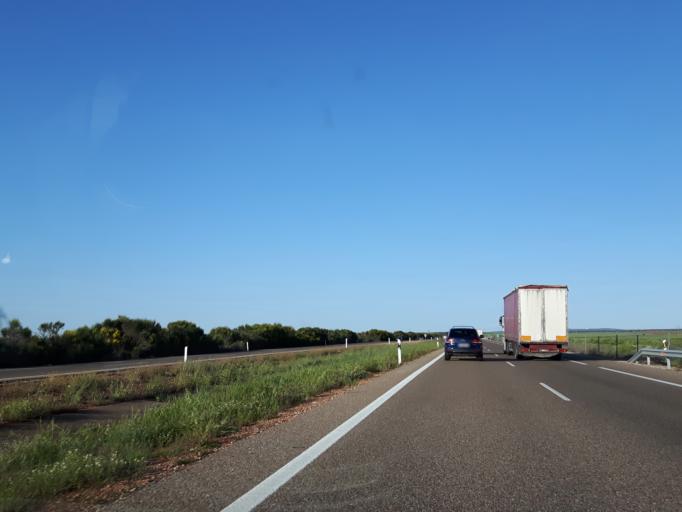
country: ES
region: Castille and Leon
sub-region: Provincia de Salamanca
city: Canillas de Abajo
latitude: 40.8901
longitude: -5.9404
